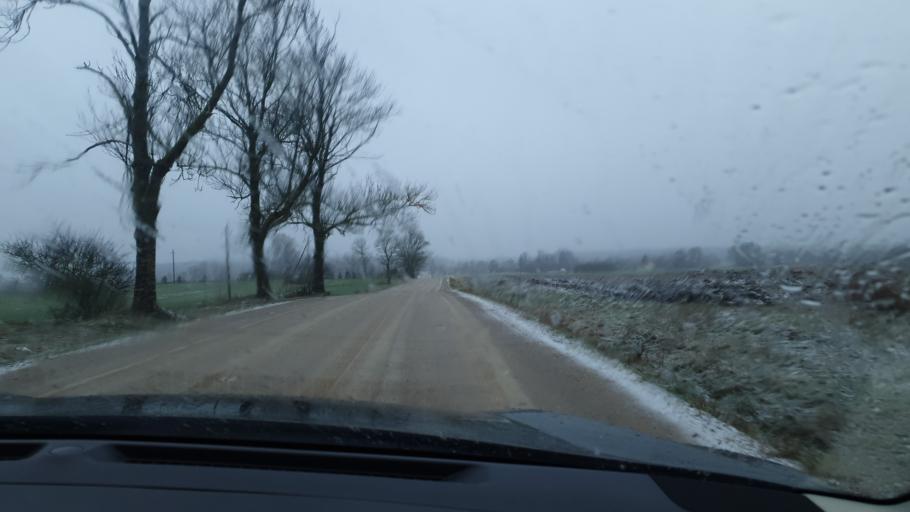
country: LT
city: Jieznas
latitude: 54.5798
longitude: 24.3168
